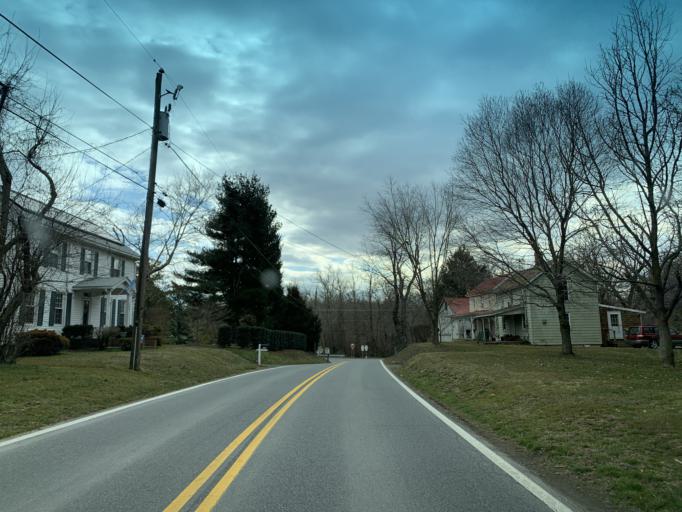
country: US
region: Maryland
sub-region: Queen Anne's County
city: Centreville
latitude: 38.9439
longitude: -76.0803
